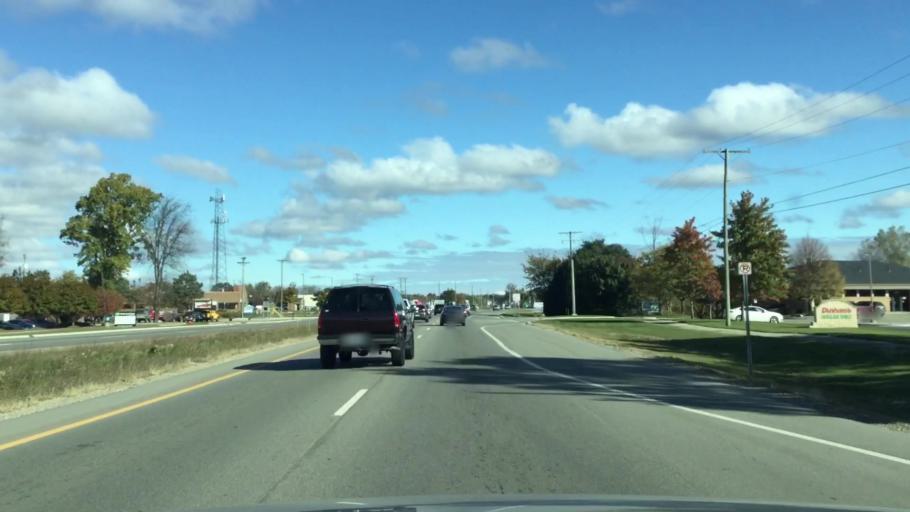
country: US
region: Michigan
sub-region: Oakland County
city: Lake Orion
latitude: 42.7625
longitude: -83.2428
